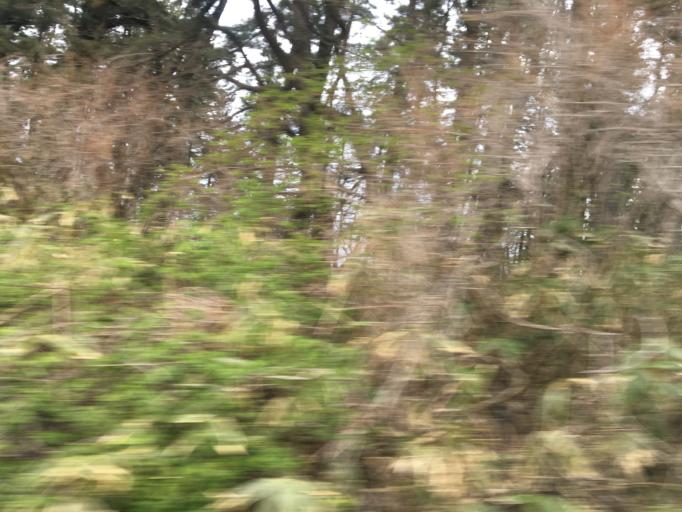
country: JP
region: Akita
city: Noshiromachi
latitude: 40.6439
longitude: 139.9057
